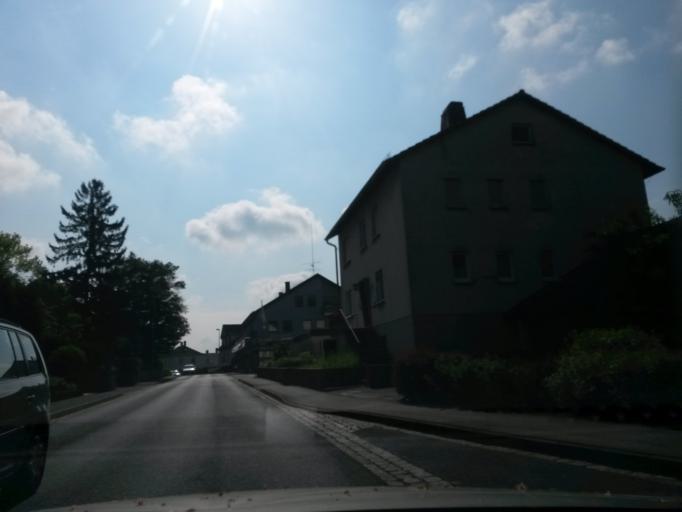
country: DE
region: Bavaria
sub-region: Regierungsbezirk Unterfranken
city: Bad Kissingen
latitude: 50.1866
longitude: 10.0868
